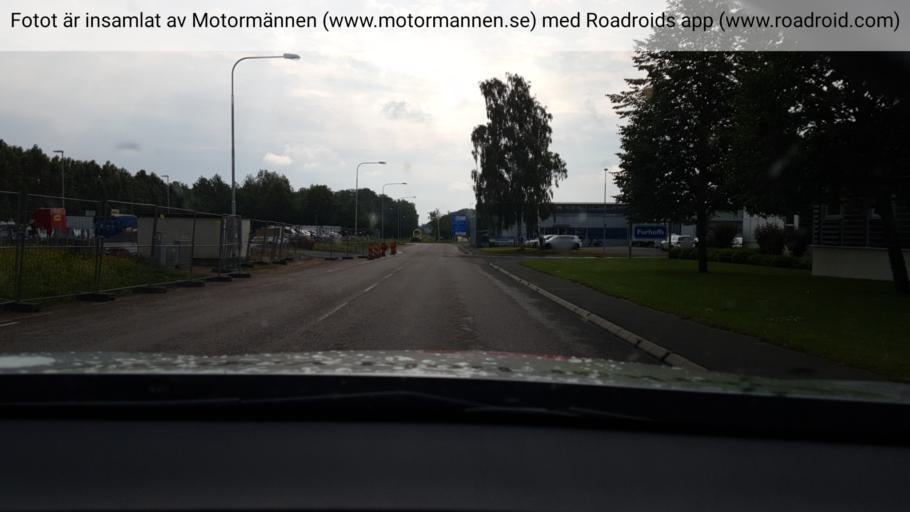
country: SE
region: Vaestra Goetaland
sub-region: Skovde Kommun
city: Skoevde
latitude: 58.3825
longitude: 13.8668
